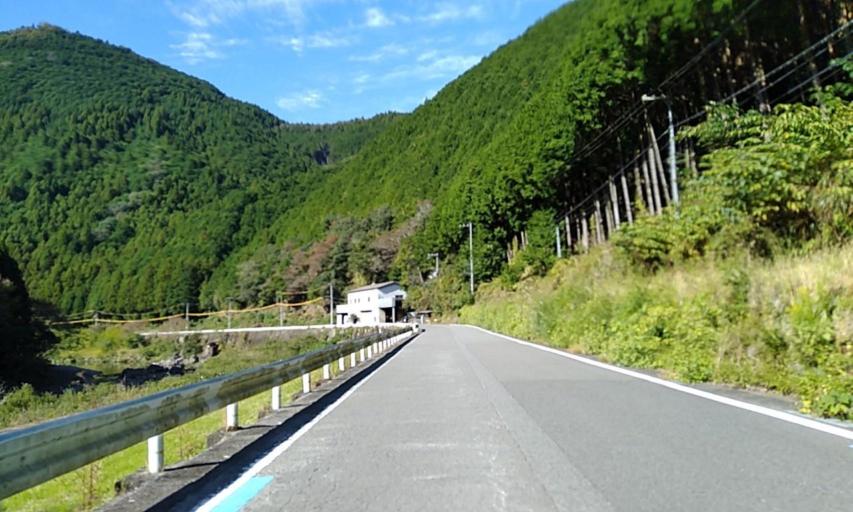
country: JP
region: Wakayama
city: Kainan
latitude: 34.0619
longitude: 135.3538
